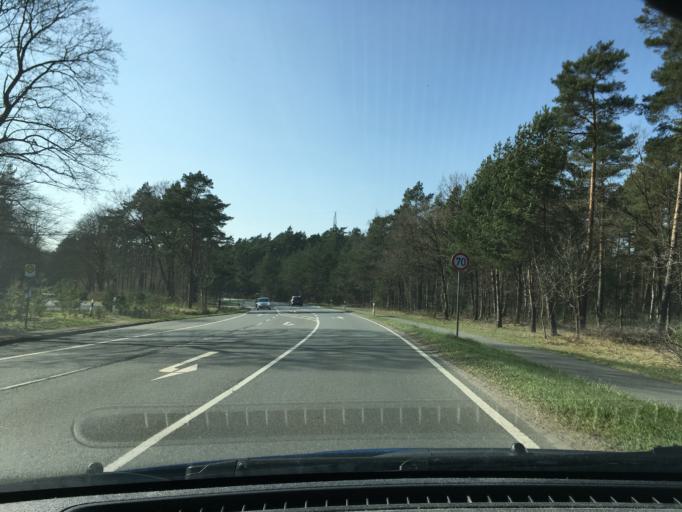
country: DE
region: Lower Saxony
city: Winsen
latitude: 52.6752
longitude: 9.9548
